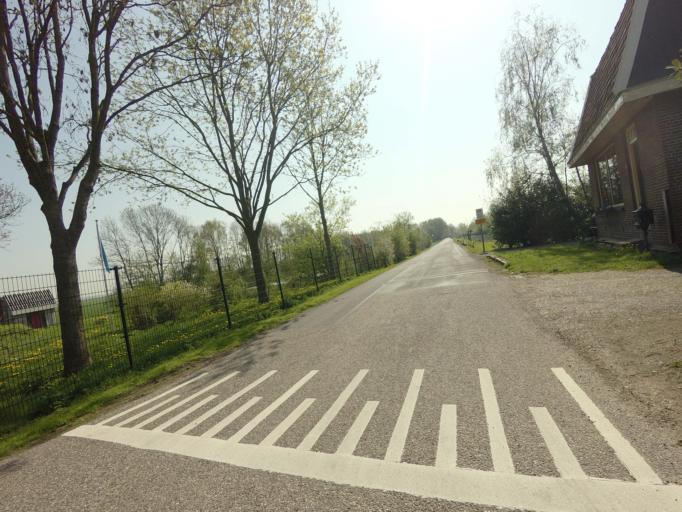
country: NL
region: Utrecht
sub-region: Gemeente De Ronde Venen
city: Mijdrecht
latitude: 52.1850
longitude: 4.8414
